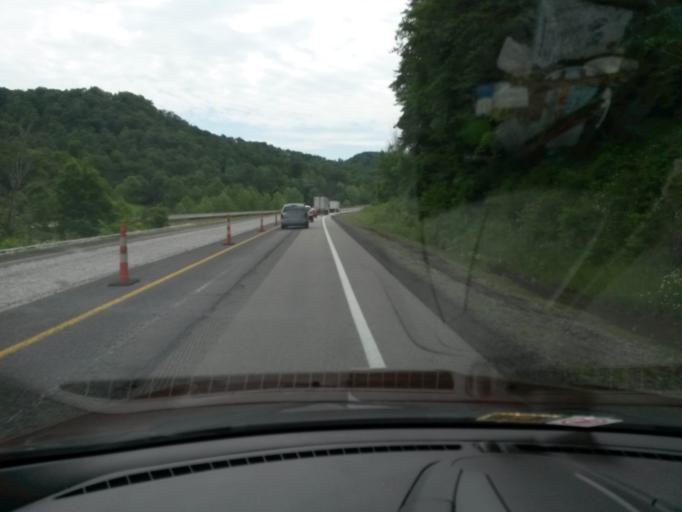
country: US
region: West Virginia
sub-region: Braxton County
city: Sutton
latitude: 38.7338
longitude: -80.6758
